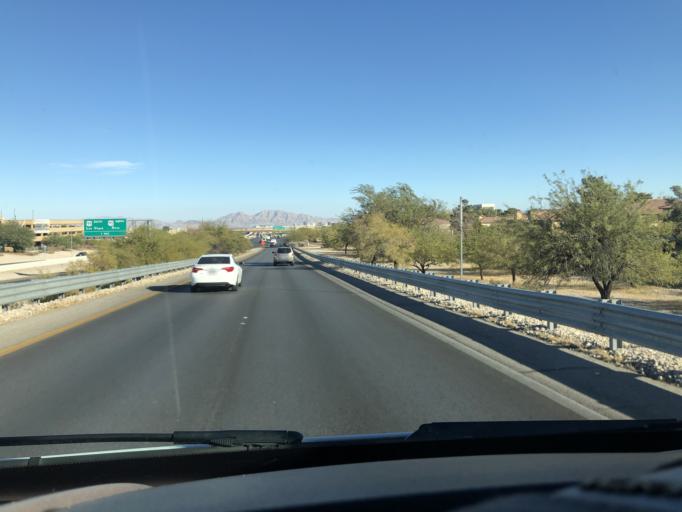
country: US
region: Nevada
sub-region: Clark County
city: Spring Valley
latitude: 36.1780
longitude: -115.2580
